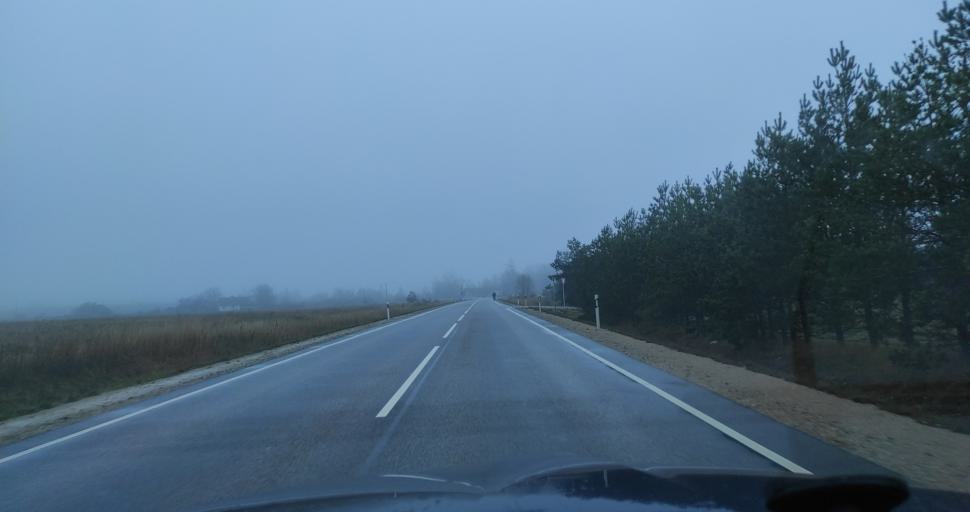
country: LV
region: Pavilostas
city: Pavilosta
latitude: 56.9394
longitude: 21.2807
